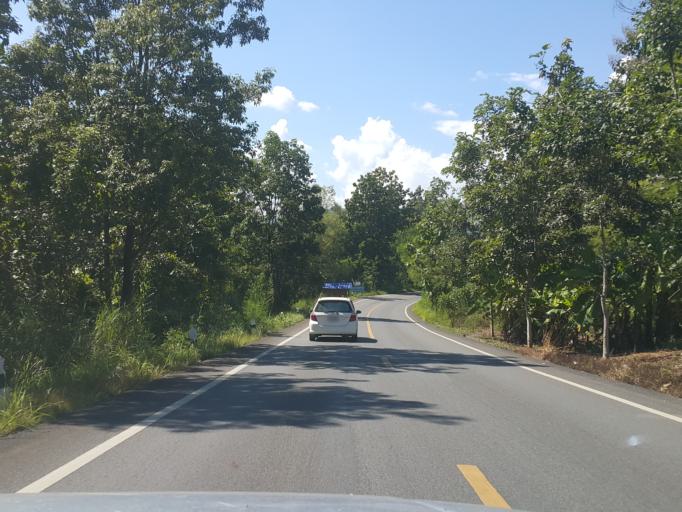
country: TH
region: Chiang Mai
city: Mae Taeng
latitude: 19.1641
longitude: 98.9345
